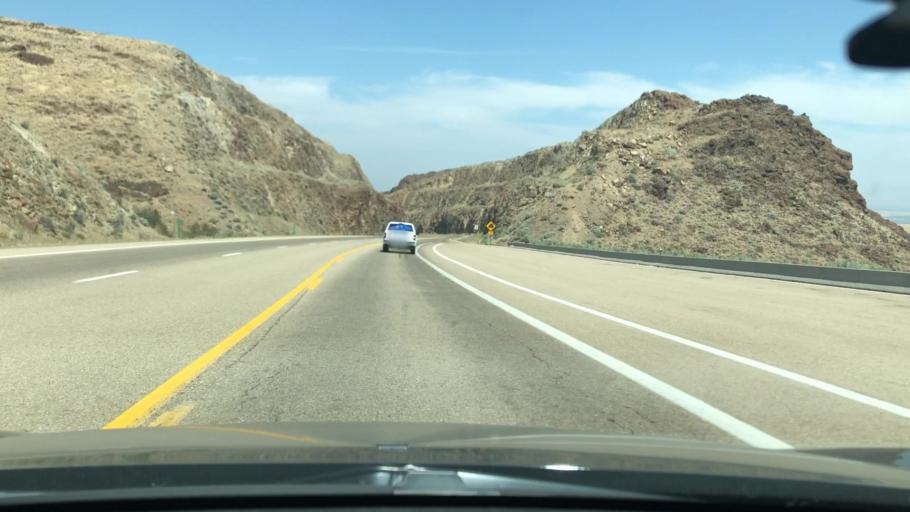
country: US
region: Idaho
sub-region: Owyhee County
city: Marsing
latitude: 43.4083
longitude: -116.8647
